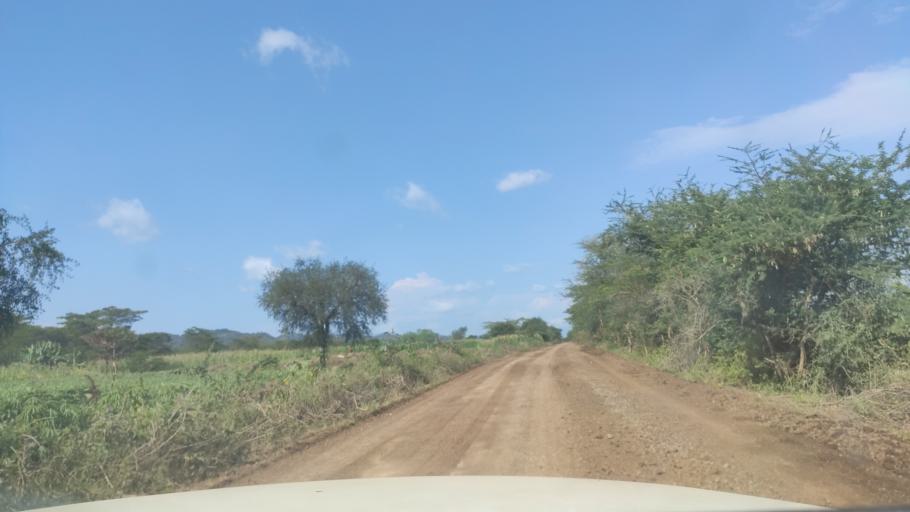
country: ET
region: Southern Nations, Nationalities, and People's Region
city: Felege Neway
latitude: 6.3784
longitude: 37.0891
